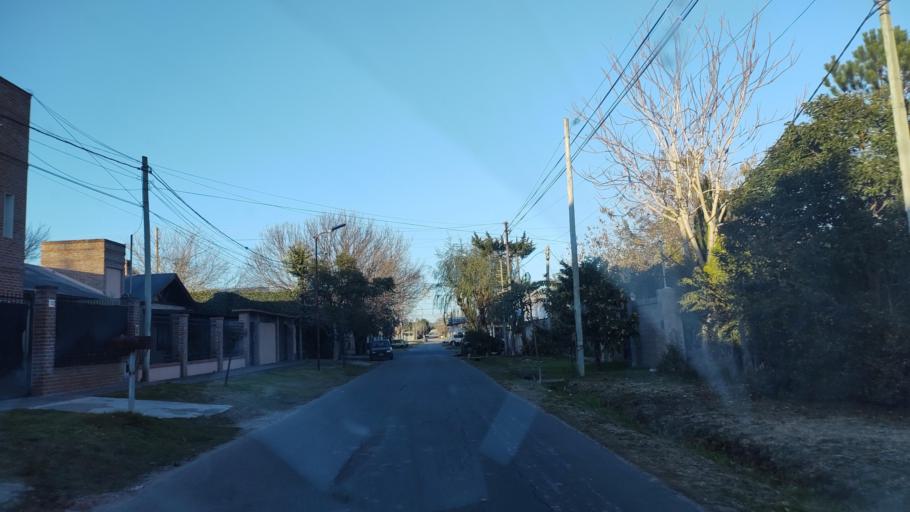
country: AR
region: Buenos Aires
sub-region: Partido de La Plata
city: La Plata
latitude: -34.8900
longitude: -58.0421
